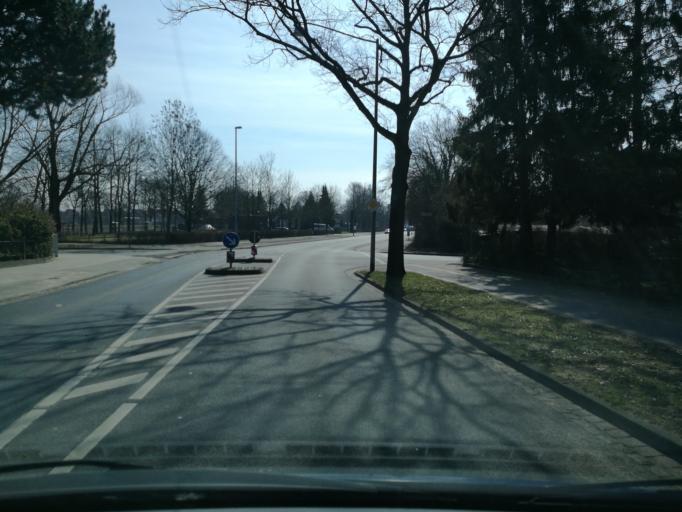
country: DE
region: Lower Saxony
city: Ronnenberg
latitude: 52.3706
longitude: 9.6696
